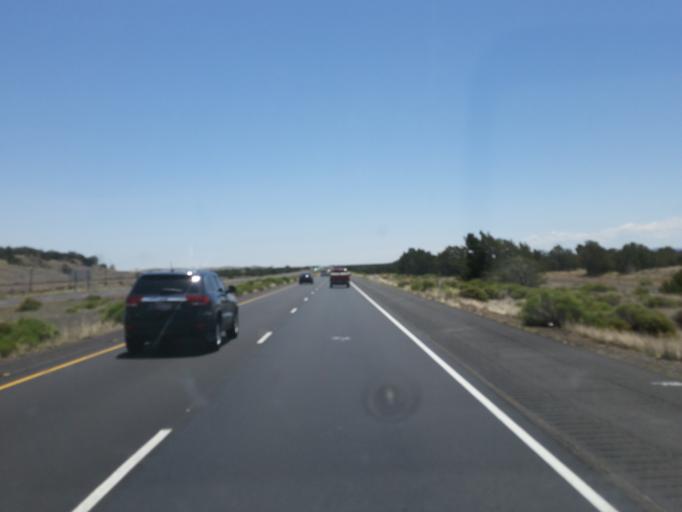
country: US
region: Arizona
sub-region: Coconino County
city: Flagstaff
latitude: 35.1953
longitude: -111.3916
